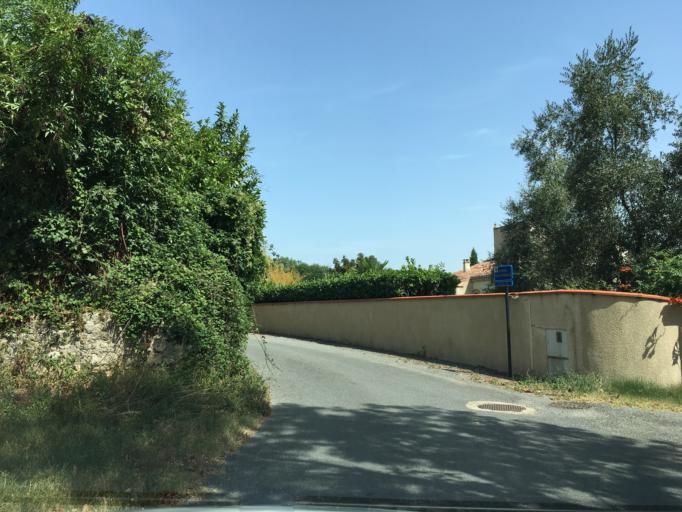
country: FR
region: Midi-Pyrenees
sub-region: Departement du Tarn
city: Roquecourbe
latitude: 43.6596
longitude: 2.2387
